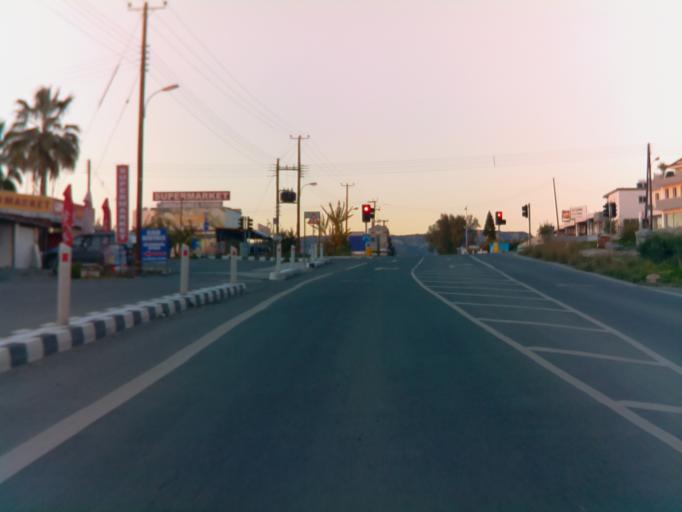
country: CY
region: Pafos
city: Kissonerga
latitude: 34.8237
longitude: 32.3924
